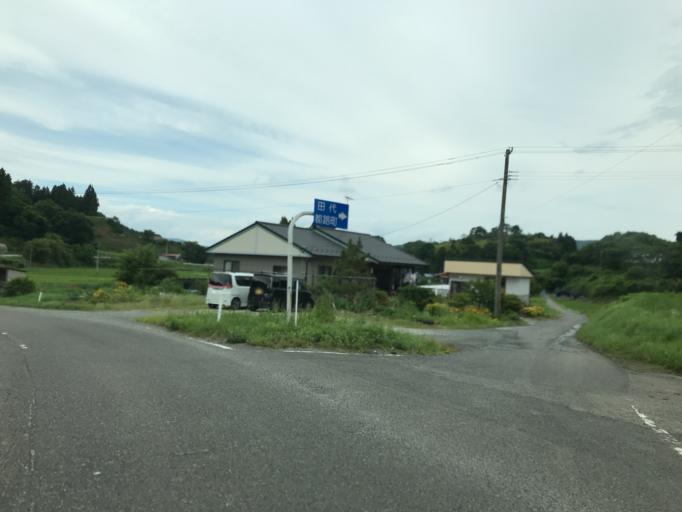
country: JP
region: Fukushima
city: Funehikimachi-funehiki
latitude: 37.4013
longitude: 140.6942
